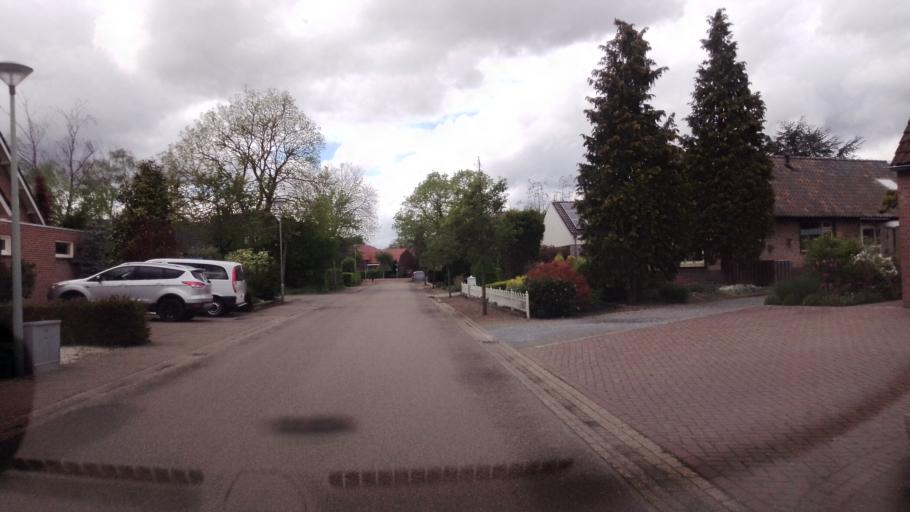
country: NL
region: Limburg
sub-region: Gemeente Bergen
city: Wellerlooi
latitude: 51.4905
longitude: 6.1196
